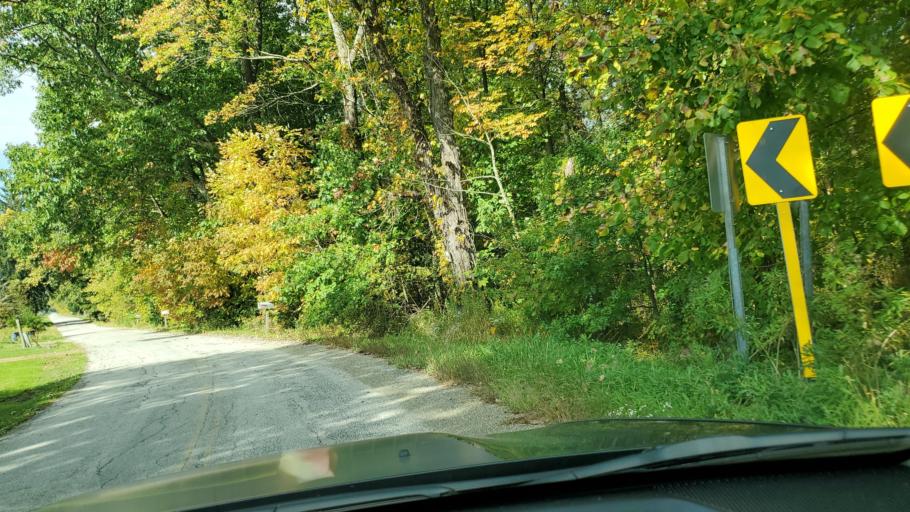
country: US
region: Ohio
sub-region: Trumbull County
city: Cortland
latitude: 41.4126
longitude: -80.6349
